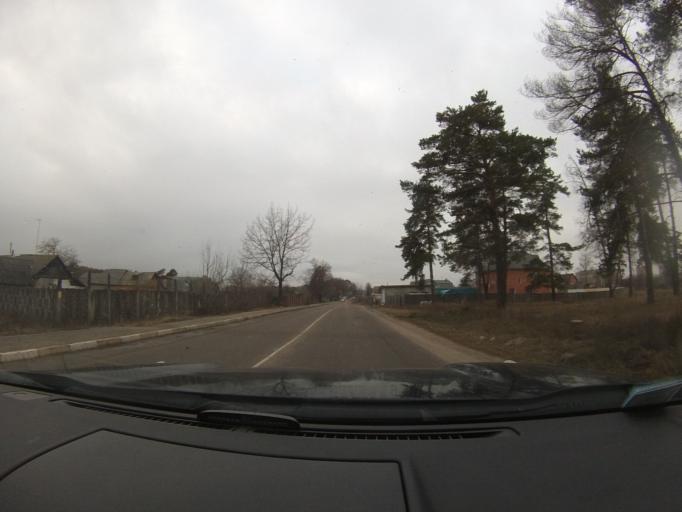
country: RU
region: Moskovskaya
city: Peski
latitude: 55.2656
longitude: 38.7580
